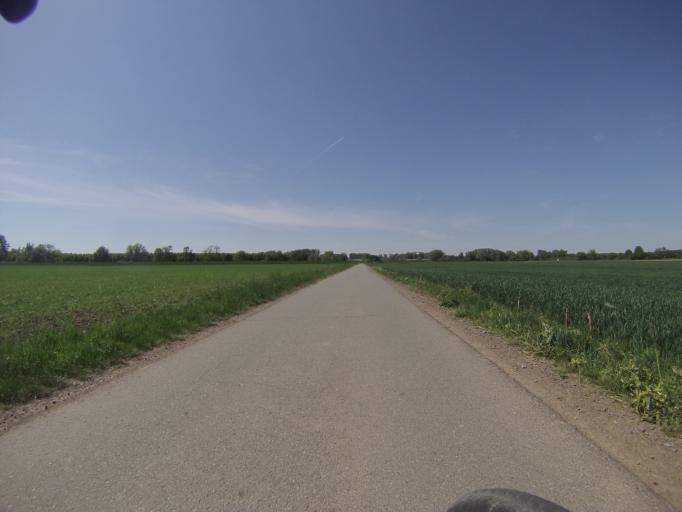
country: CZ
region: South Moravian
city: Novosedly
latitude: 48.8174
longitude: 16.4723
